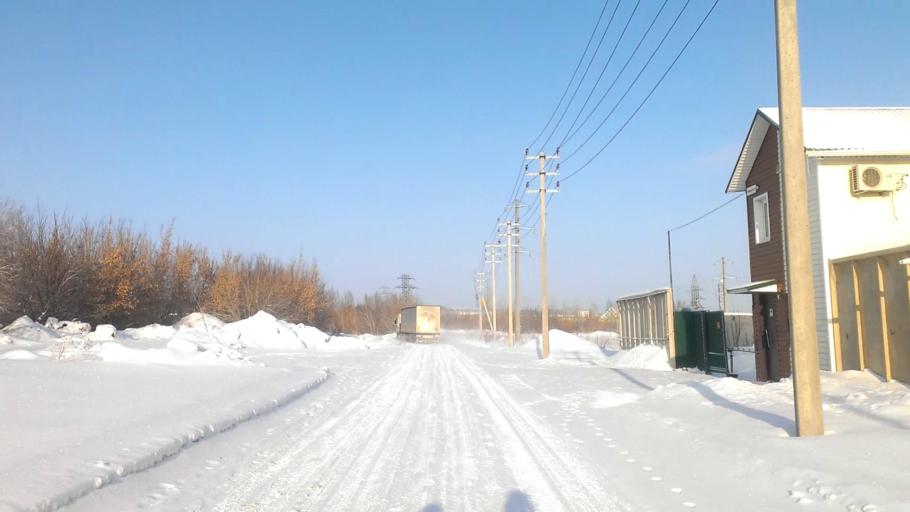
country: RU
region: Altai Krai
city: Novosilikatnyy
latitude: 53.3440
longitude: 83.6299
